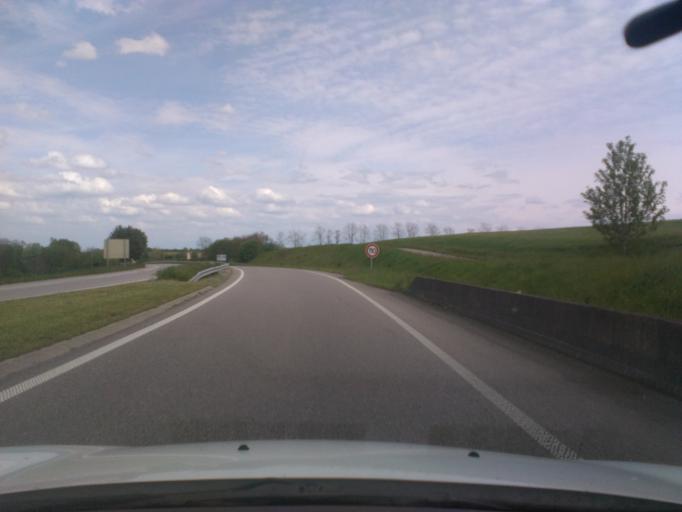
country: FR
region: Lorraine
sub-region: Departement des Vosges
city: Mirecourt
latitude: 48.2183
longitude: 6.2180
